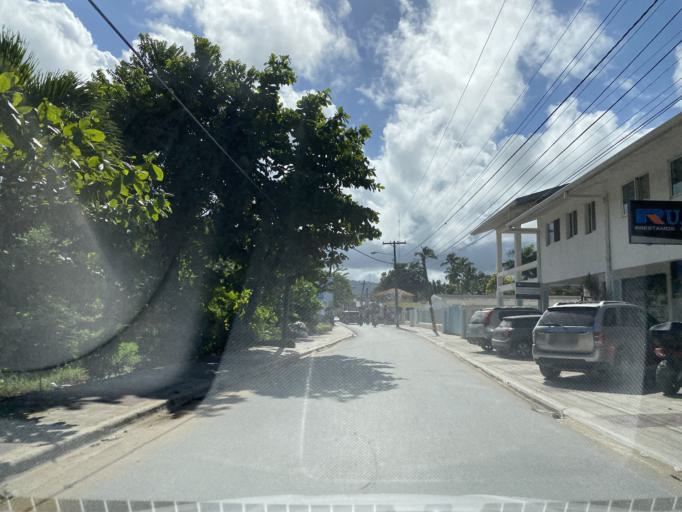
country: DO
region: Samana
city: Las Terrenas
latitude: 19.3202
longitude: -69.5405
